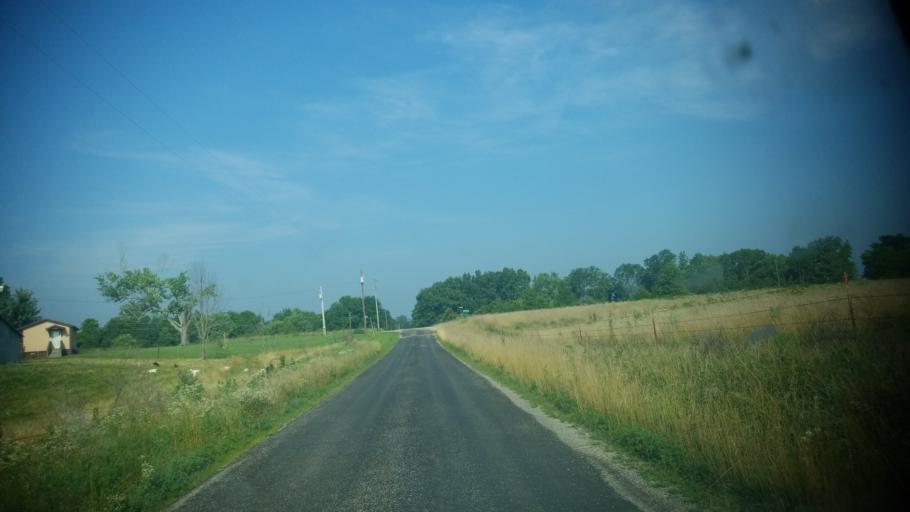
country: US
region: Illinois
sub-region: Clay County
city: Flora
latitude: 38.6028
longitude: -88.4000
